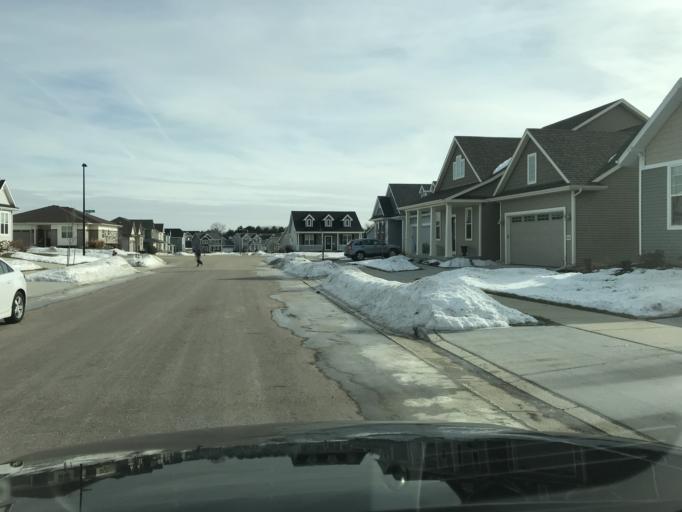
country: US
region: Wisconsin
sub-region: Dane County
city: Monona
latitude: 43.0935
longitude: -89.2768
